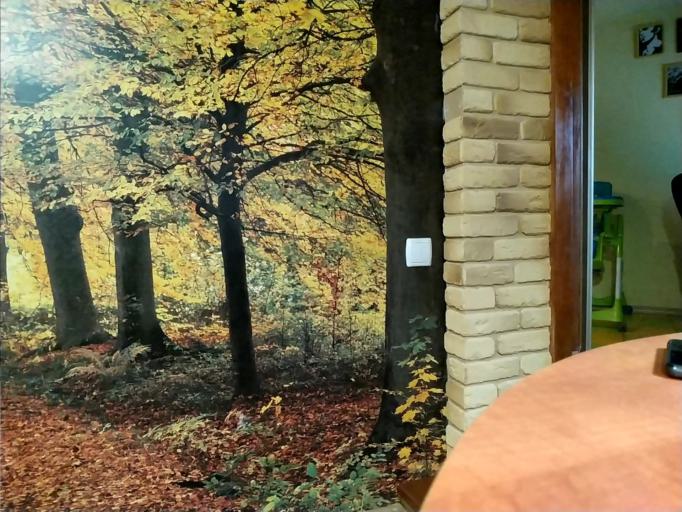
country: BY
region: Minsk
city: Il'ya
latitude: 54.4234
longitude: 27.5001
